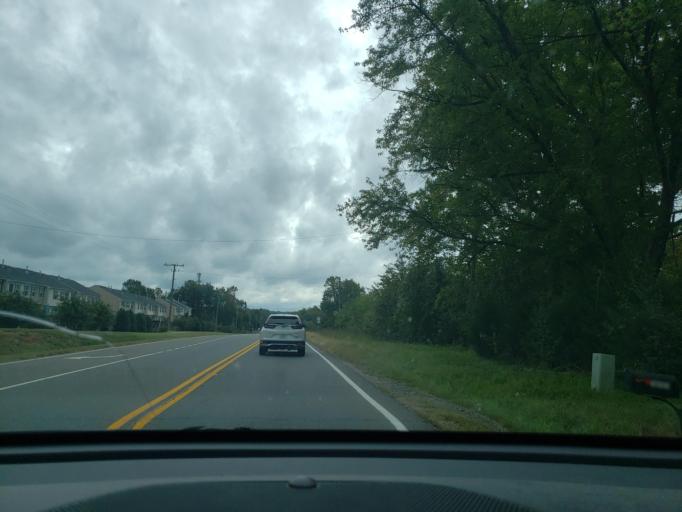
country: US
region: Virginia
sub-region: City of Fredericksburg
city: Fredericksburg
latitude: 38.2427
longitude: -77.4180
